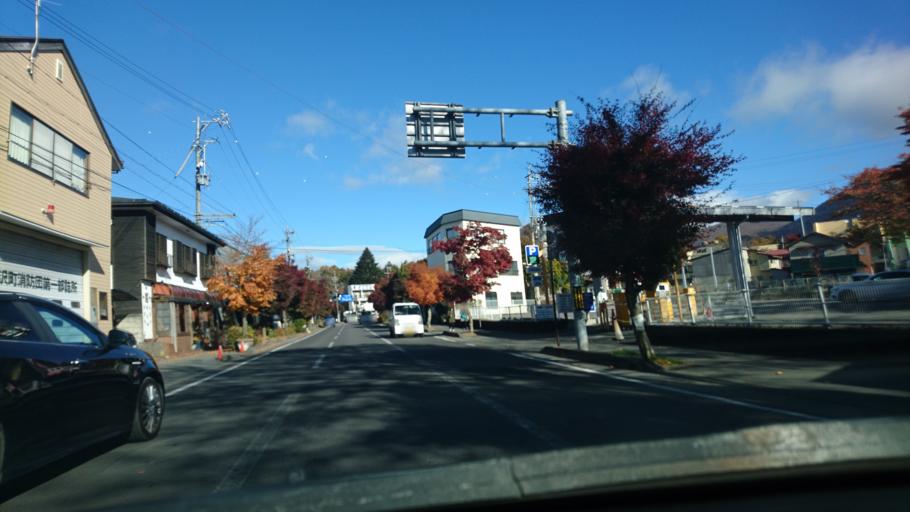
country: JP
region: Nagano
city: Komoro
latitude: 36.3579
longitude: 138.6339
